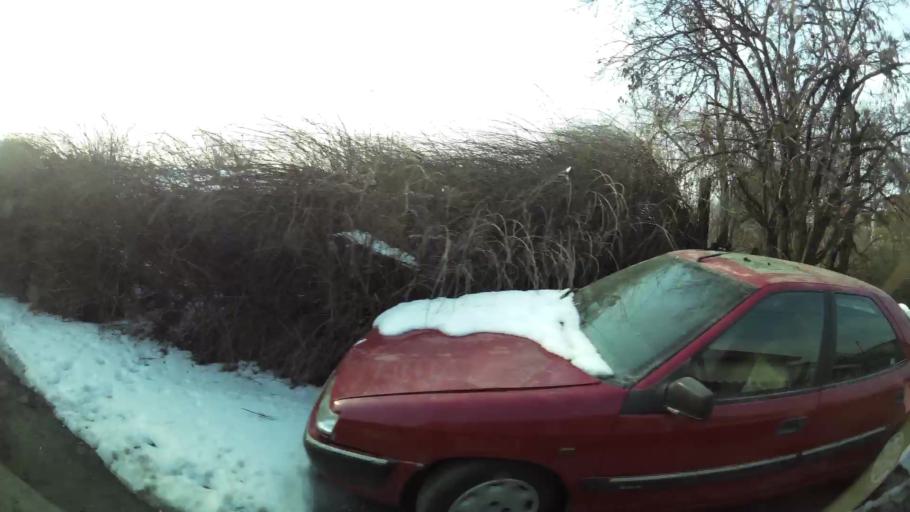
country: MK
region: Karpos
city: Skopje
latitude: 42.0141
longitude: 21.4115
